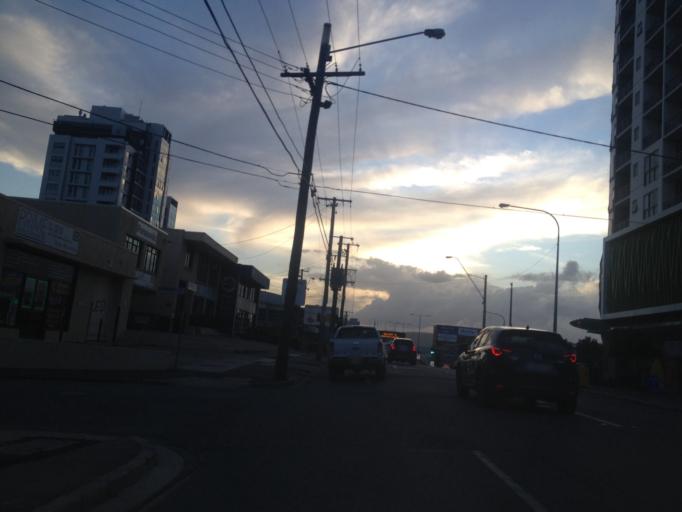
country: AU
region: Queensland
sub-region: Brisbane
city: Fortitude Valley
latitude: -27.4477
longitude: 153.0368
